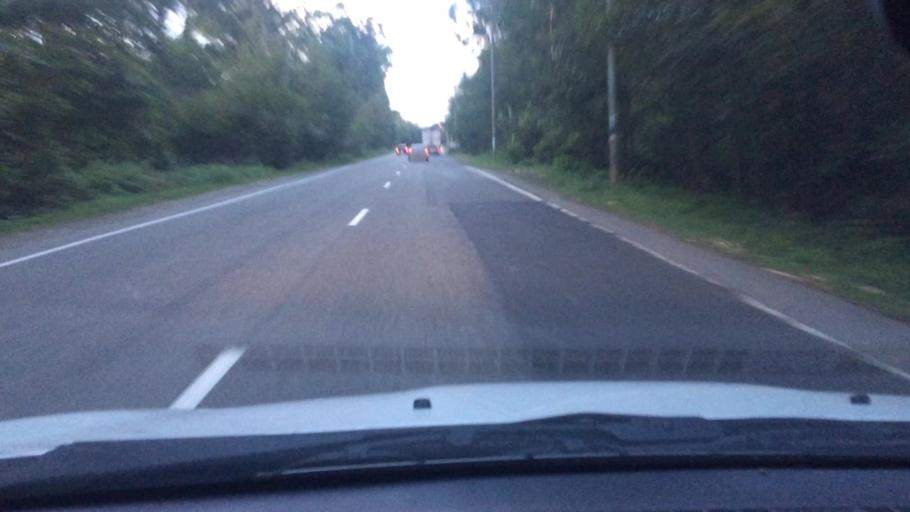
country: GE
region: Guria
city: Urek'i
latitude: 41.9742
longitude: 41.7822
